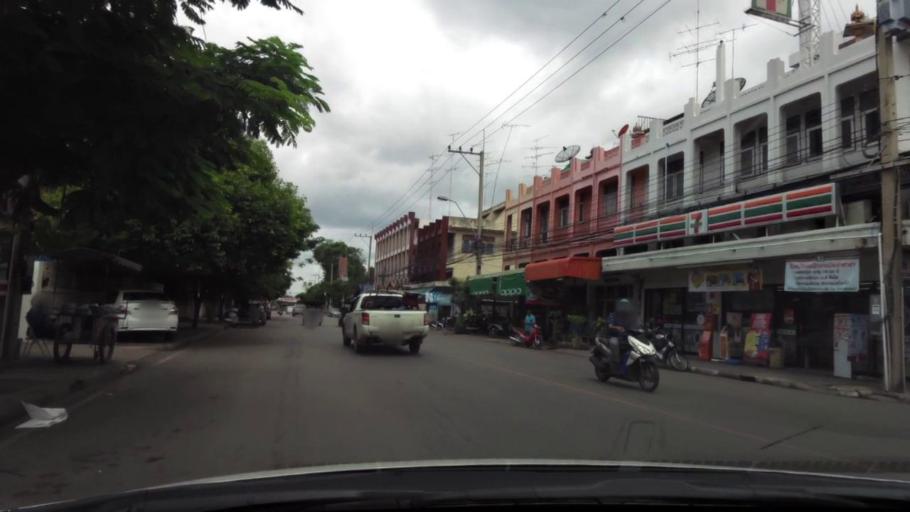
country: TH
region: Ratchaburi
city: Ratchaburi
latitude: 13.5377
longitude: 99.8308
